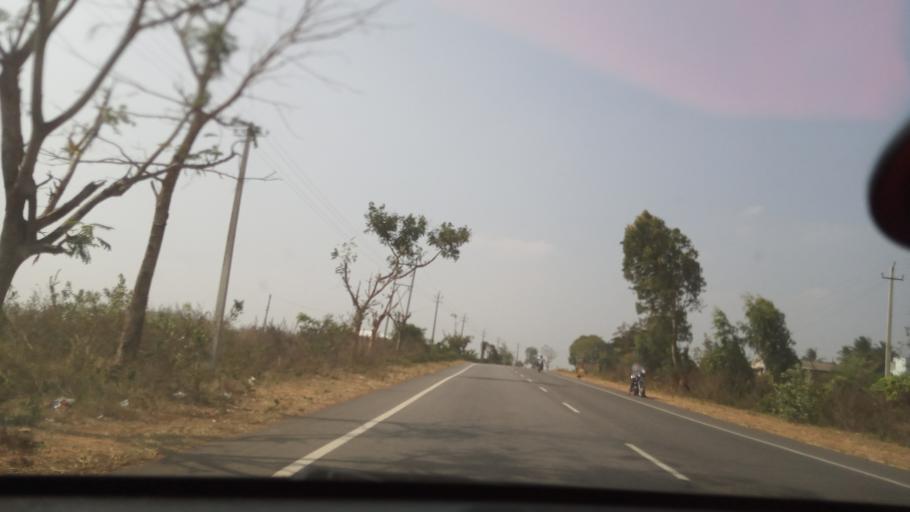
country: IN
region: Karnataka
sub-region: Mysore
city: Nanjangud
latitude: 12.0921
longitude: 76.7236
